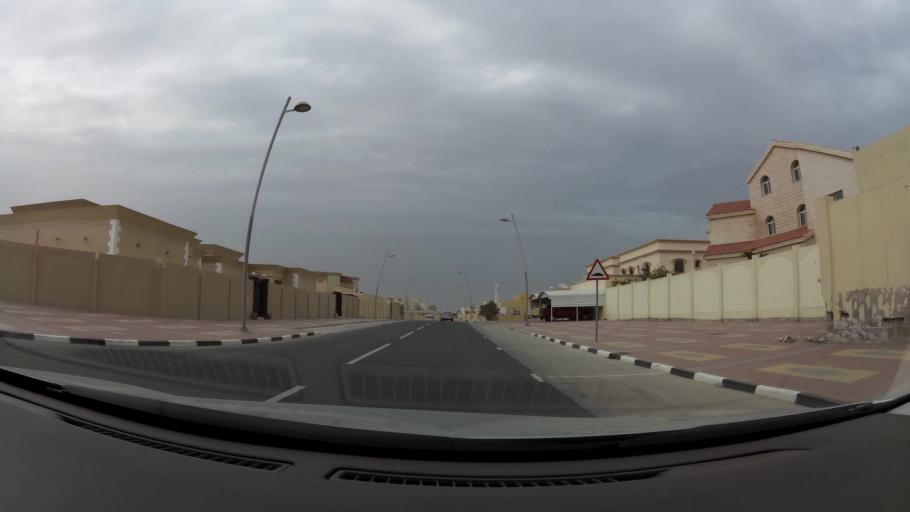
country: QA
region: Baladiyat ad Dawhah
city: Doha
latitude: 25.3422
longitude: 51.4878
